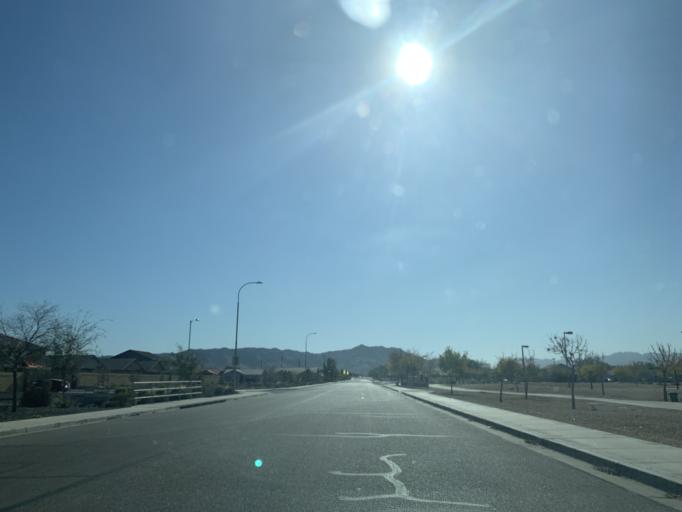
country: US
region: Arizona
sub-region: Maricopa County
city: Laveen
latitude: 33.3979
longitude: -112.1253
